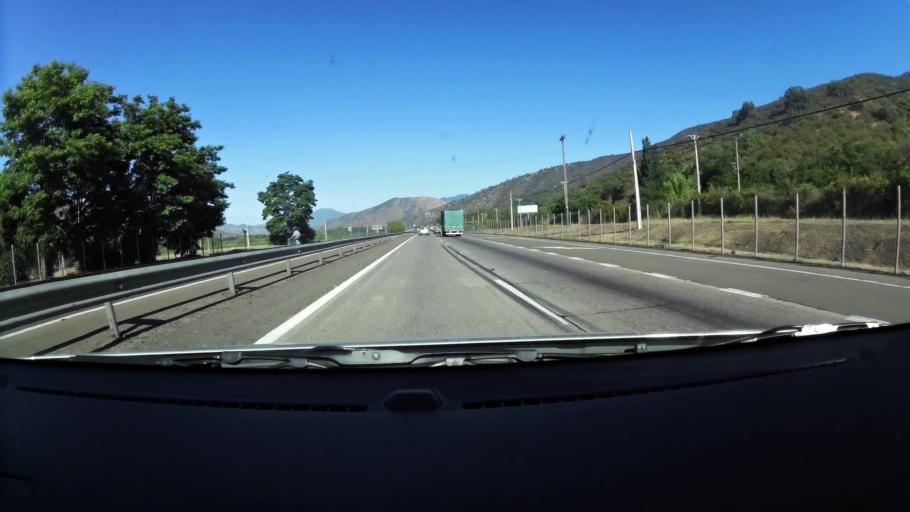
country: CL
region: Santiago Metropolitan
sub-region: Provincia de Chacabuco
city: Lampa
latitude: -33.4048
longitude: -71.0859
